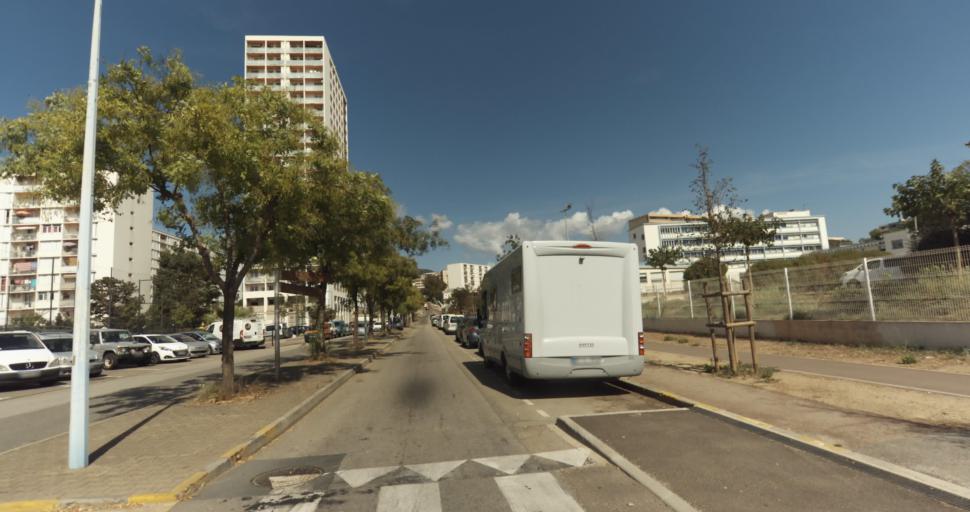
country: FR
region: Corsica
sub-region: Departement de la Corse-du-Sud
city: Ajaccio
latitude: 41.9359
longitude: 8.7509
